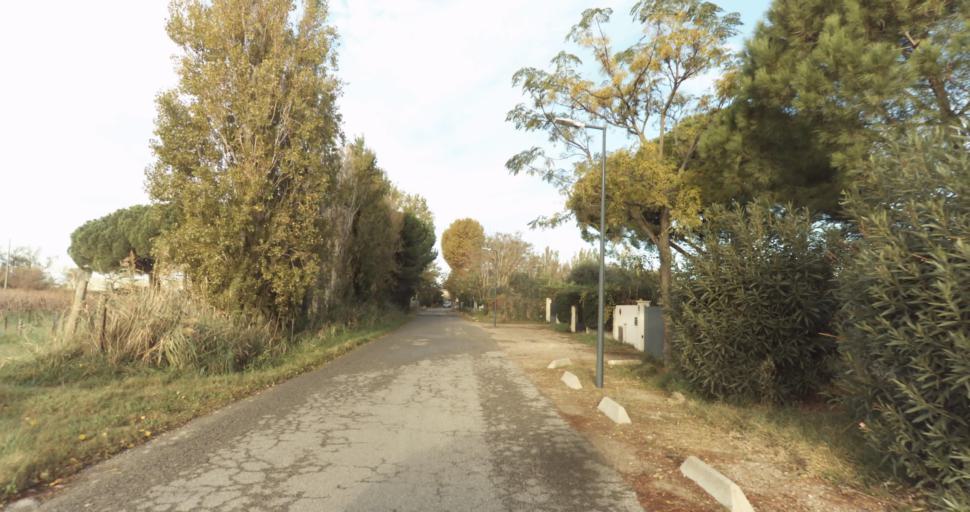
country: FR
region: Languedoc-Roussillon
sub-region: Departement du Gard
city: Aigues-Mortes
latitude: 43.5642
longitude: 4.1989
